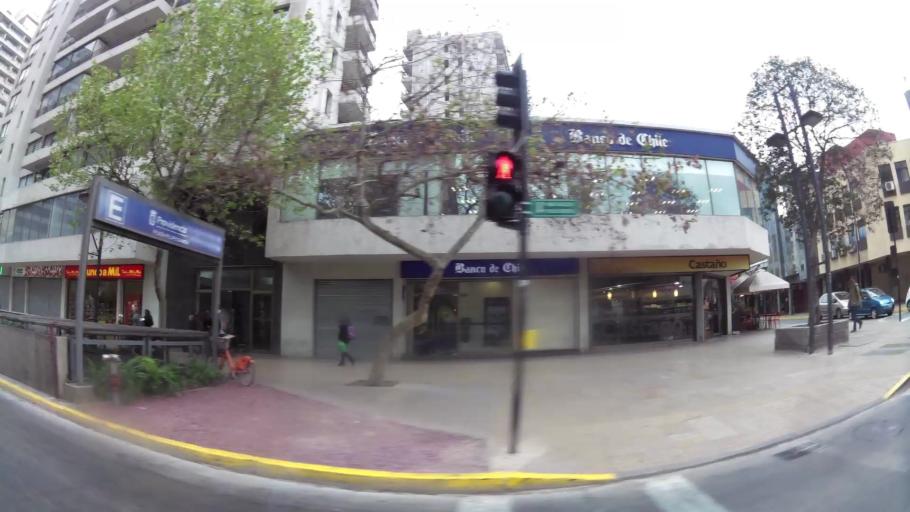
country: CL
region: Santiago Metropolitan
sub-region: Provincia de Santiago
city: Santiago
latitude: -33.4288
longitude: -70.6185
